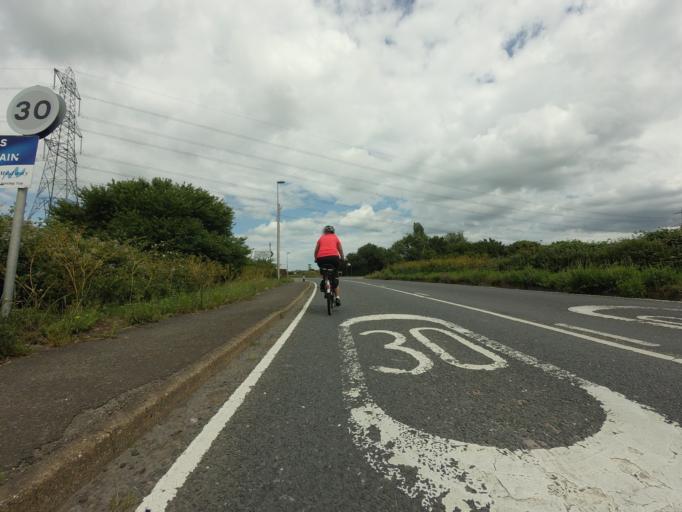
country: GB
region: England
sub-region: Kent
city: Sheerness
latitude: 51.4538
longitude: 0.7074
